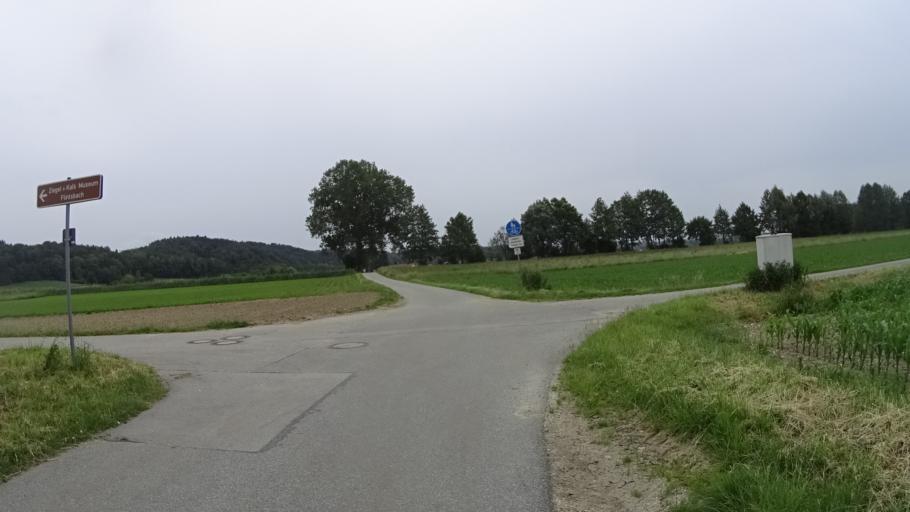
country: DE
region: Bavaria
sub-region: Lower Bavaria
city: Winzer
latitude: 48.7121
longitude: 13.1011
